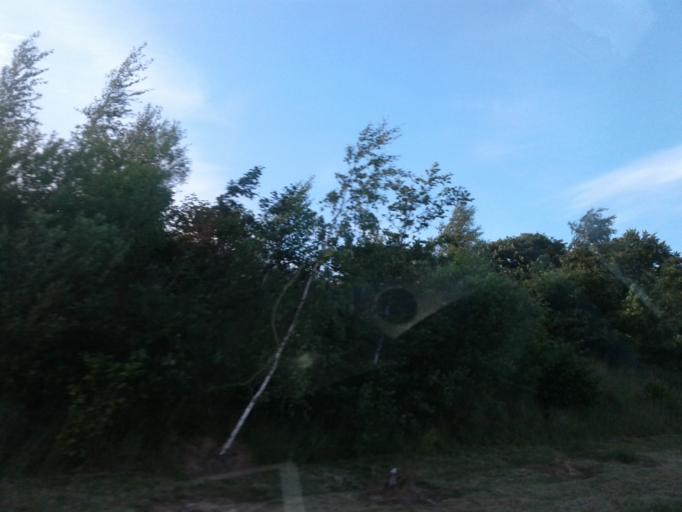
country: IE
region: Connaught
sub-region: County Galway
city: Ballinasloe
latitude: 53.3155
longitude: -8.2462
